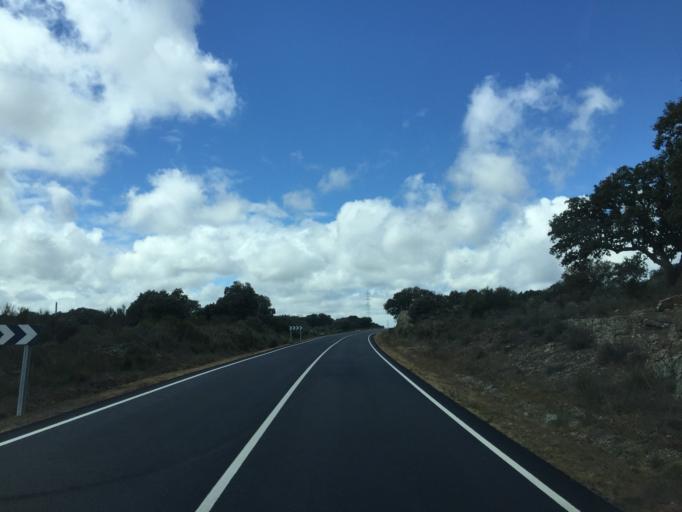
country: ES
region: Castille and Leon
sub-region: Provincia de Zamora
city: Moral de Sayago
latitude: 41.4831
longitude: -6.1148
